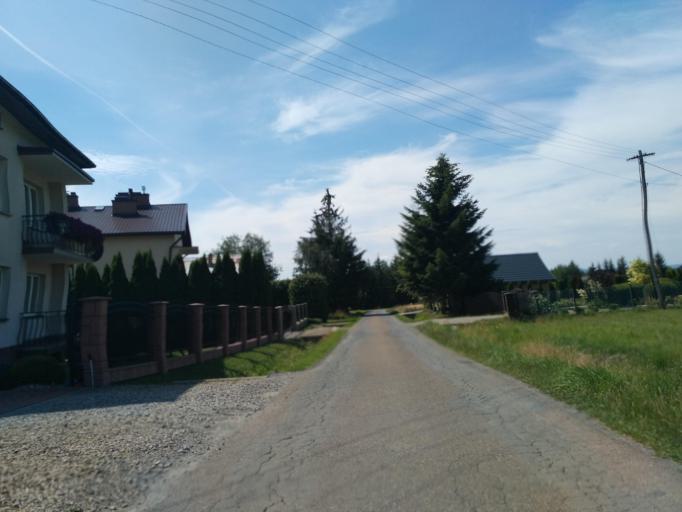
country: PL
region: Subcarpathian Voivodeship
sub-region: Powiat krosnienski
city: Korczyna
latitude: 49.7120
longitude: 21.8287
